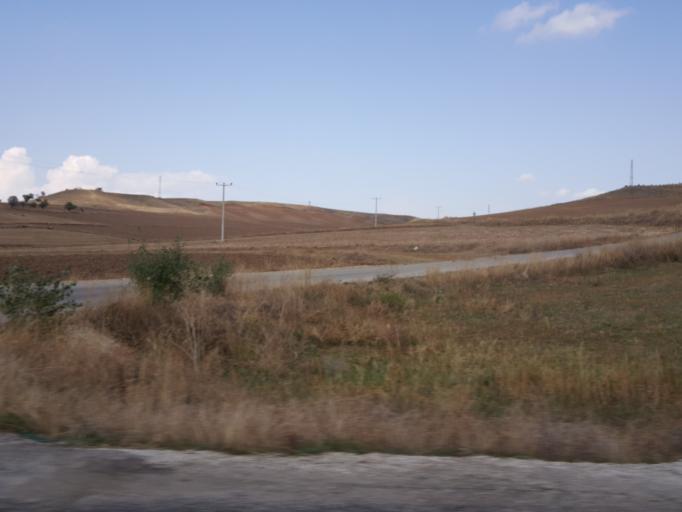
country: TR
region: Corum
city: Alaca
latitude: 40.1575
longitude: 34.7097
